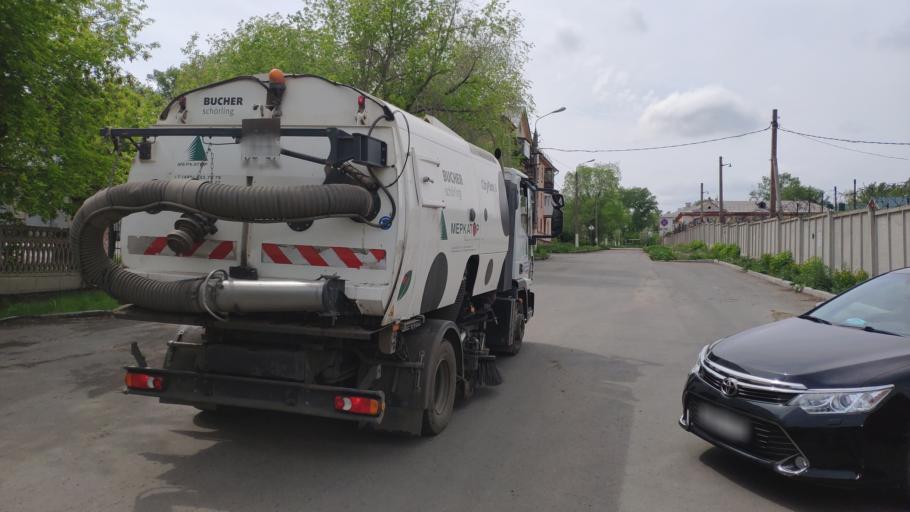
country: RU
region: Chelyabinsk
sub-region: Gorod Magnitogorsk
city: Magnitogorsk
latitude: 53.4189
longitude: 58.9596
